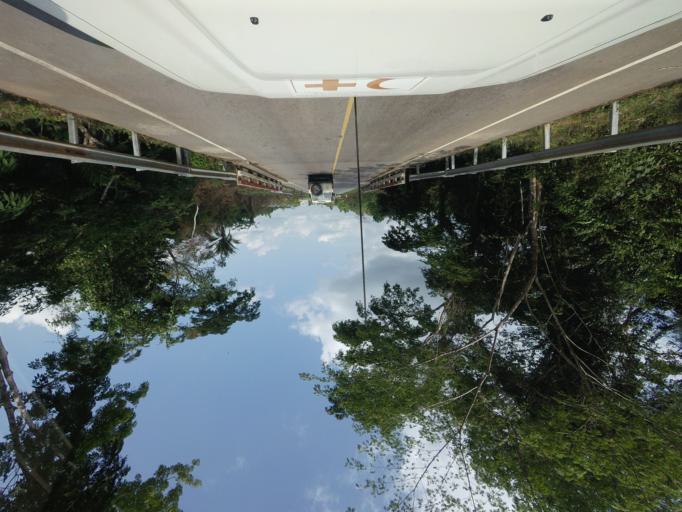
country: LR
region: Bong
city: Gbarnga
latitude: 6.8497
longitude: -9.7940
